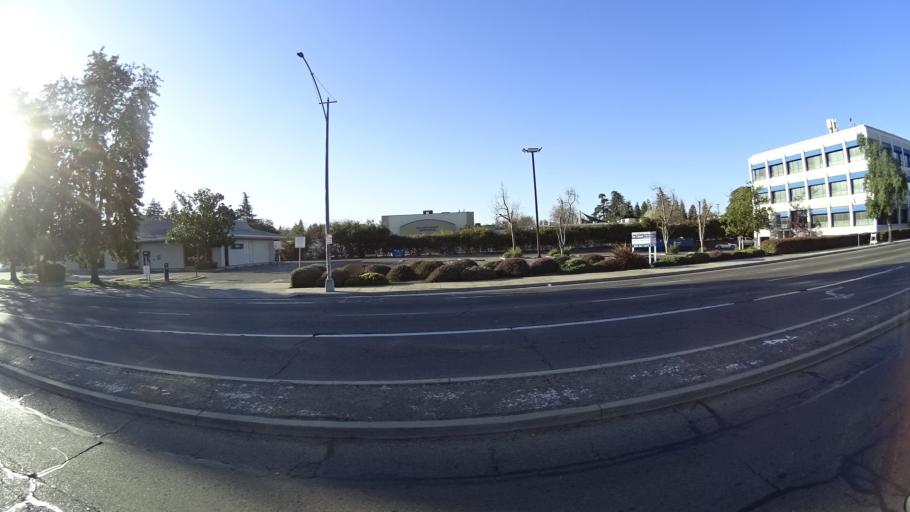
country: US
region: California
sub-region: Fresno County
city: Fresno
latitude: 36.8085
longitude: -119.8093
